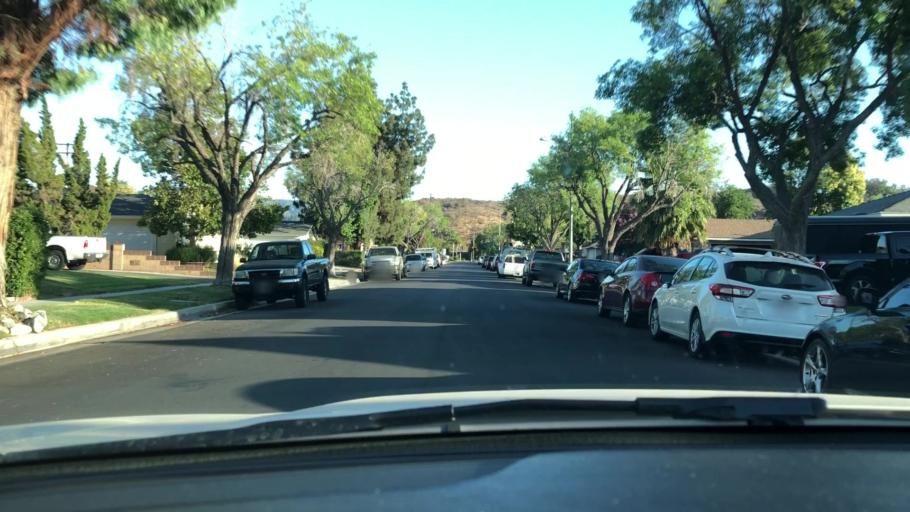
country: US
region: California
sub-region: Los Angeles County
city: Santa Clarita
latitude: 34.4230
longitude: -118.4845
